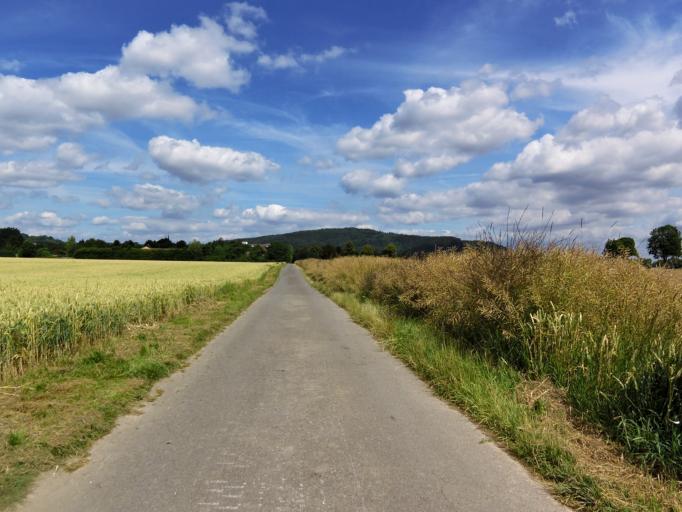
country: DE
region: North Rhine-Westphalia
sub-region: Regierungsbezirk Detmold
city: Hoexter
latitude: 51.7664
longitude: 9.3905
